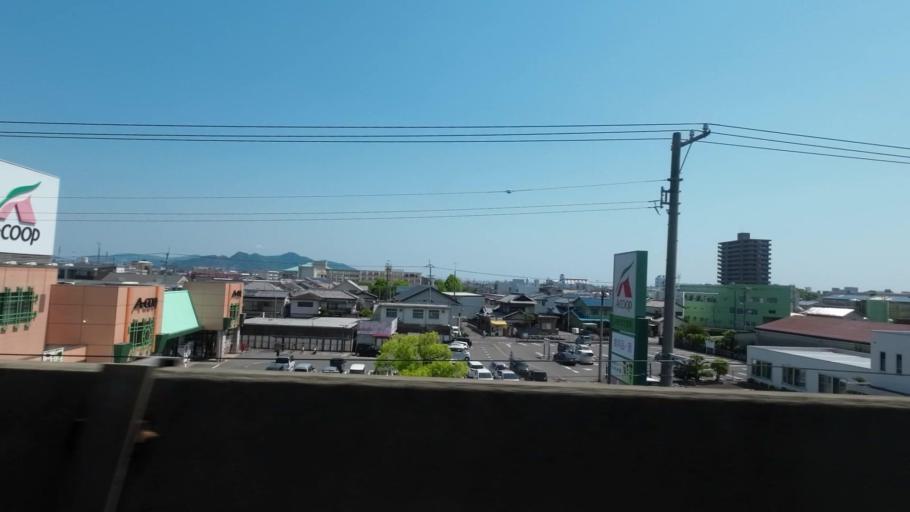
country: JP
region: Ehime
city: Hojo
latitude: 34.0689
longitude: 132.9894
